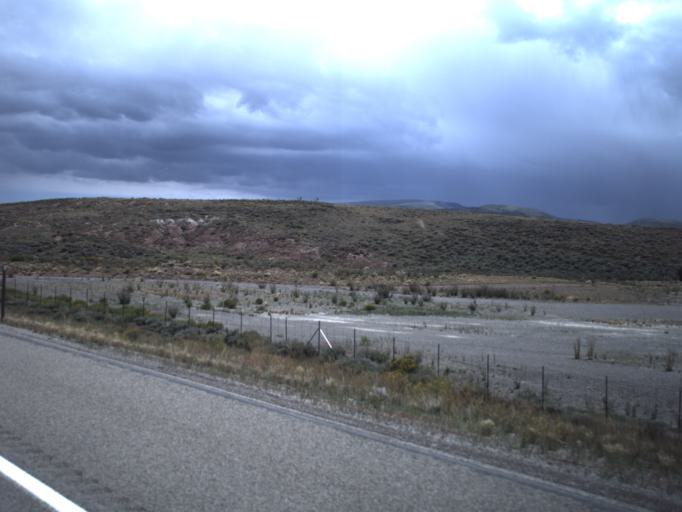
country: US
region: Utah
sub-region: Carbon County
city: Helper
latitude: 39.8467
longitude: -111.0050
